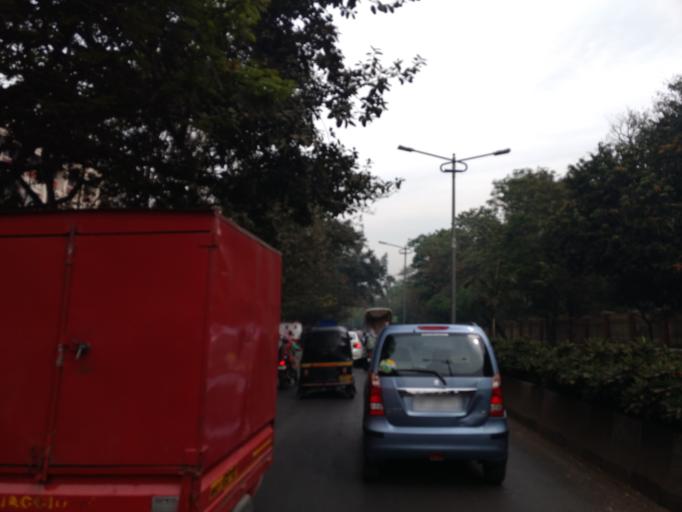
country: IN
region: Maharashtra
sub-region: Pune Division
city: Pune
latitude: 18.5251
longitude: 73.8788
